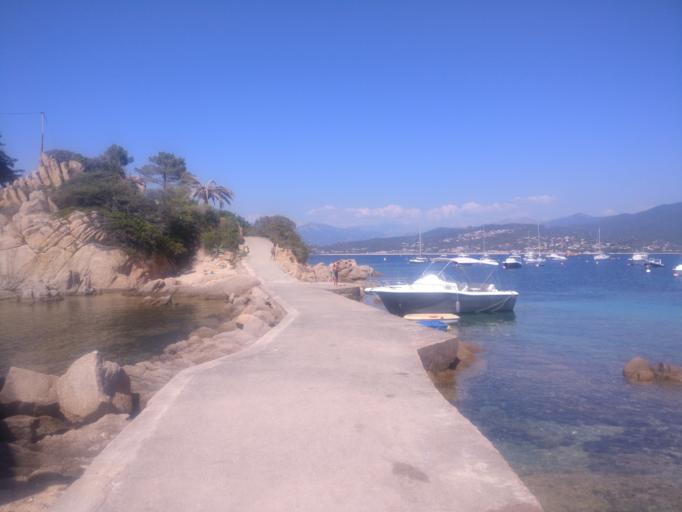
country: FR
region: Corsica
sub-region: Departement de la Corse-du-Sud
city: Ajaccio
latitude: 41.8483
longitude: 8.7608
